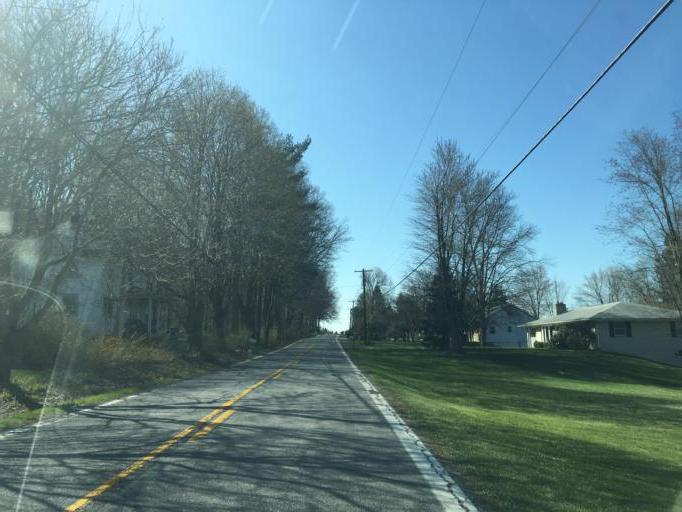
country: US
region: Maryland
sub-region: Washington County
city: Cavetown
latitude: 39.5884
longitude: -77.5579
